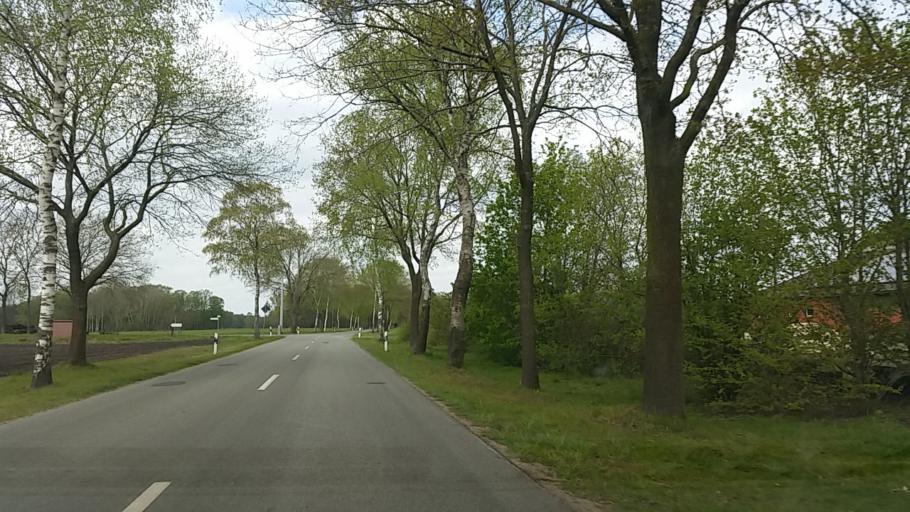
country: DE
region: Lower Saxony
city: Konigsmoor
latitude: 53.1975
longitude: 9.7127
